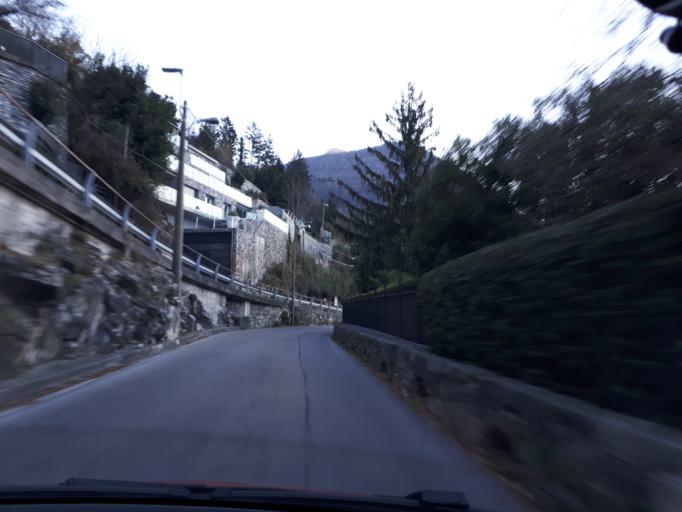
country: IT
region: Lombardy
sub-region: Provincia di Como
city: Nesso
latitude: 45.9127
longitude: 9.1547
